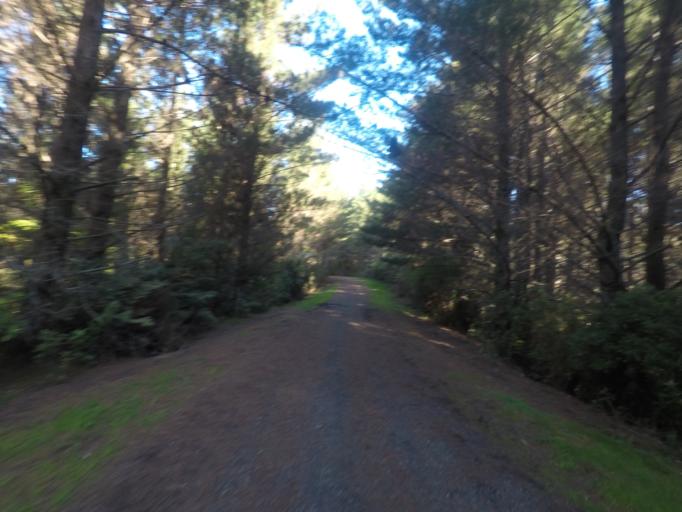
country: NZ
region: Auckland
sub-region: Auckland
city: Muriwai Beach
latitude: -36.7459
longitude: 174.5582
